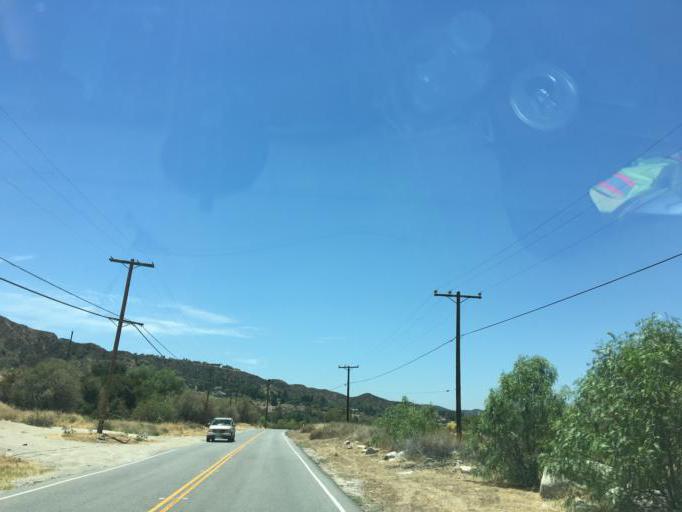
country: US
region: California
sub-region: Los Angeles County
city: La Crescenta-Montrose
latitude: 34.2880
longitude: -118.2908
